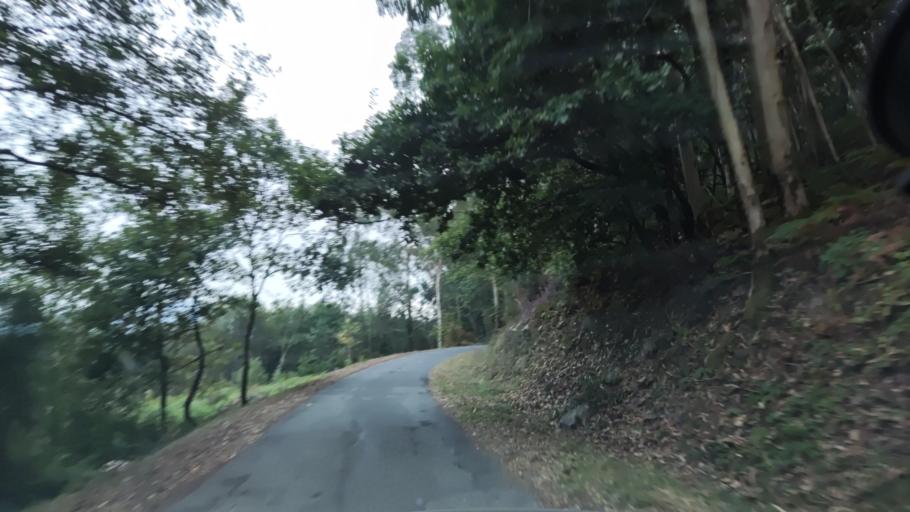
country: ES
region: Galicia
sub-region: Provincia de Pontevedra
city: Catoira
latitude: 42.6997
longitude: -8.7269
